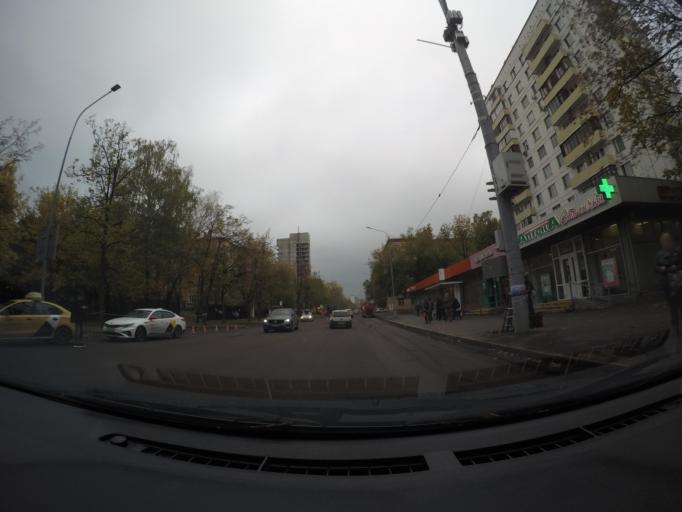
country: RU
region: Moskovskaya
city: Izmaylovo
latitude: 55.7634
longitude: 37.7918
